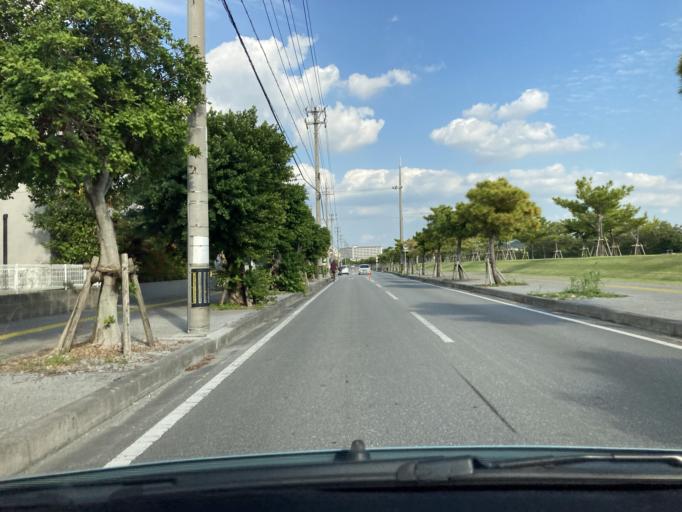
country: JP
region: Okinawa
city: Itoman
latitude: 26.1525
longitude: 127.6616
